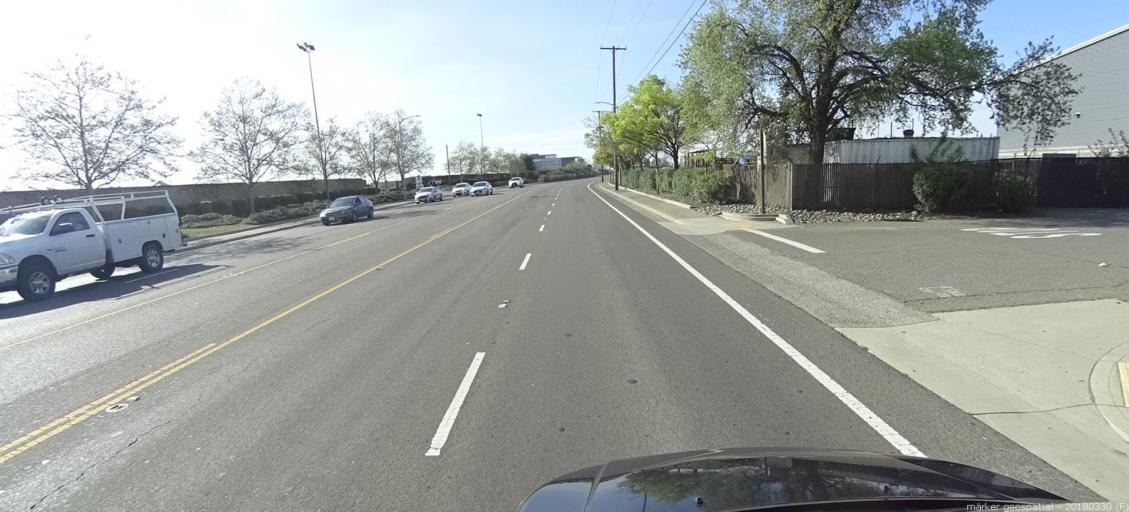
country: US
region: California
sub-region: Sacramento County
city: La Riviera
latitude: 38.5487
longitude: -121.3353
